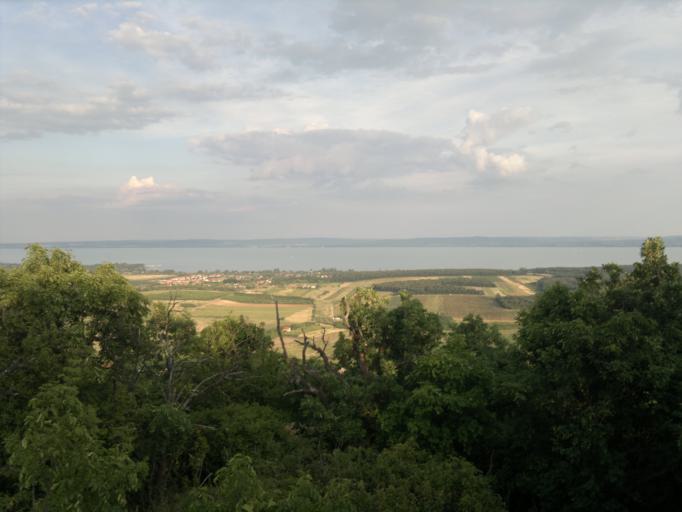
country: HU
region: Veszprem
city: Zanka
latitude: 46.8891
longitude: 17.6482
